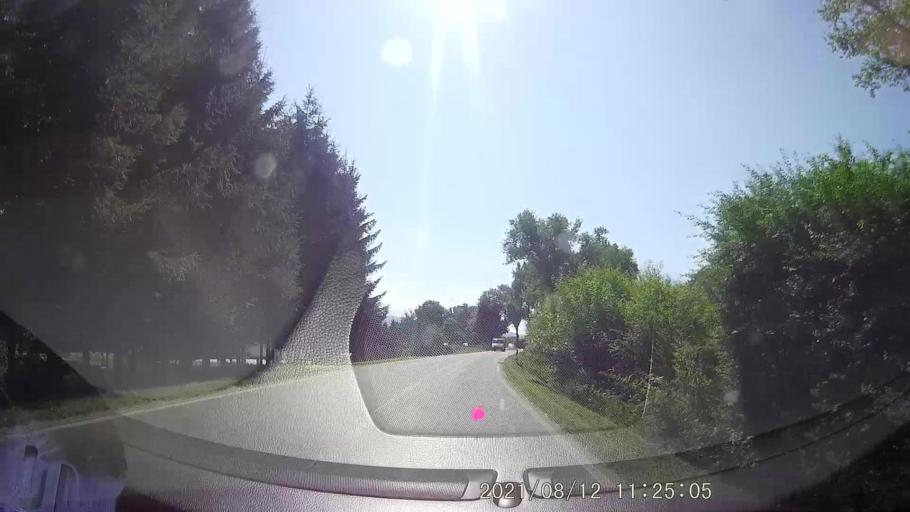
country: PL
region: Lower Silesian Voivodeship
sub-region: Powiat klodzki
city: Bystrzyca Klodzka
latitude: 50.2884
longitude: 16.6763
